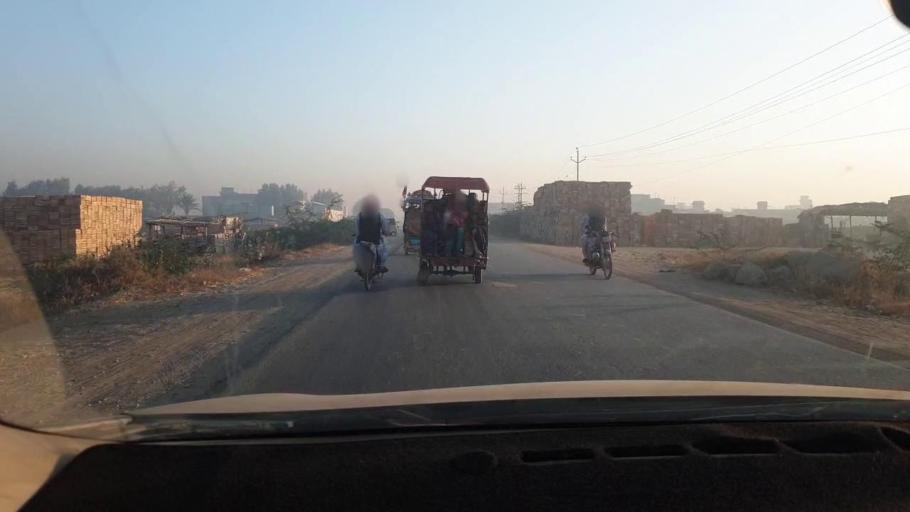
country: PK
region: Sindh
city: Malir Cantonment
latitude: 25.0008
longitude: 67.1483
